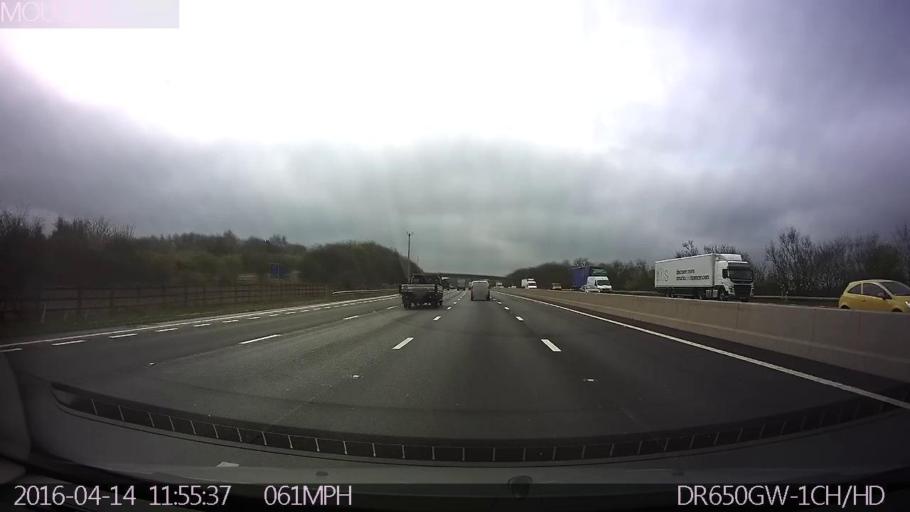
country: GB
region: England
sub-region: Derbyshire
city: Tibshelf
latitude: 53.1423
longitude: -1.3310
